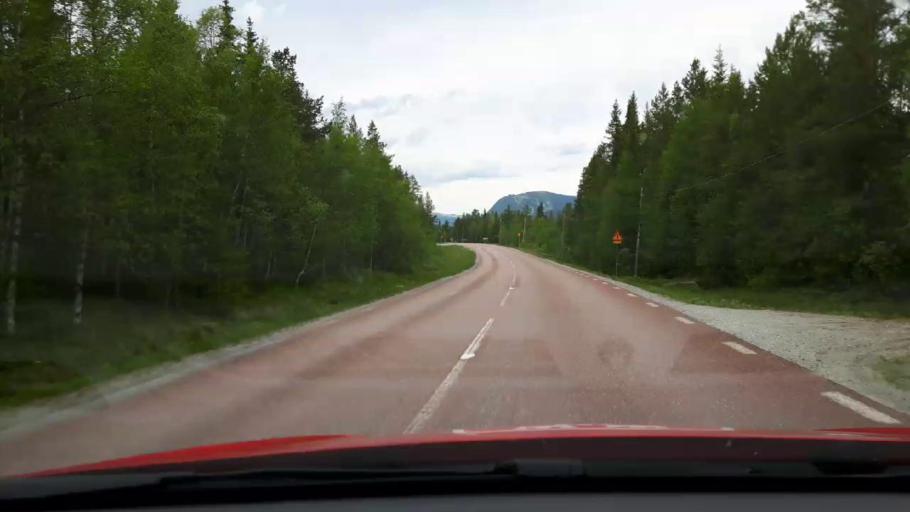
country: NO
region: Hedmark
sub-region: Engerdal
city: Engerdal
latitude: 62.5021
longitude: 12.6250
